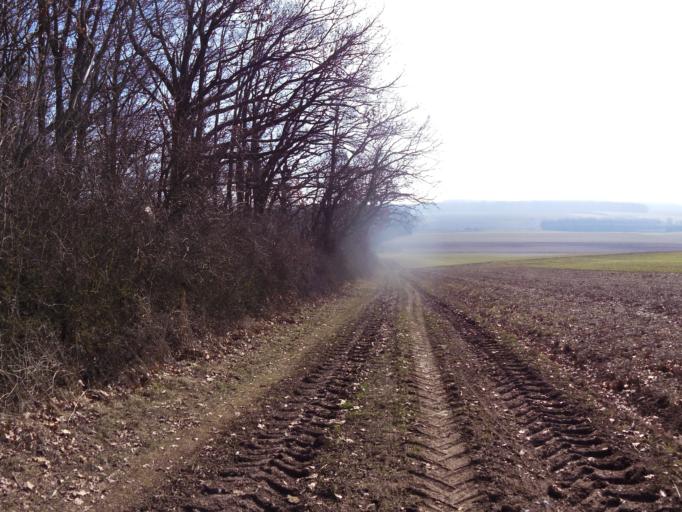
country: DE
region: Bavaria
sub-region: Regierungsbezirk Unterfranken
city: Kurnach
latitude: 49.8274
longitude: 10.0370
